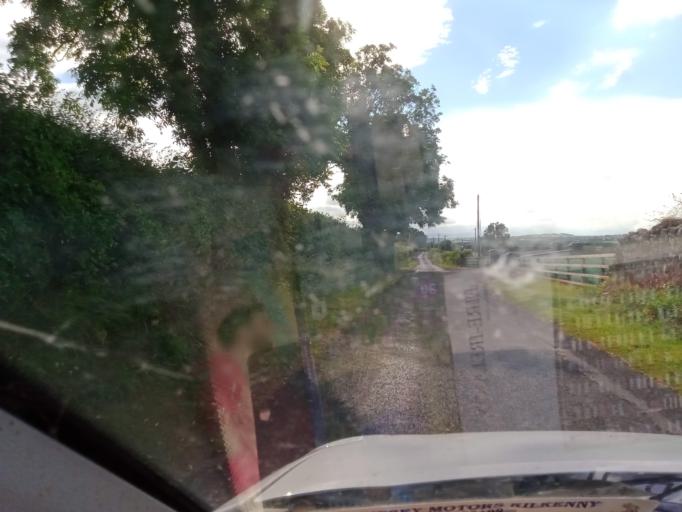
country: IE
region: Leinster
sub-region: Laois
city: Rathdowney
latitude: 52.7724
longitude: -7.5049
